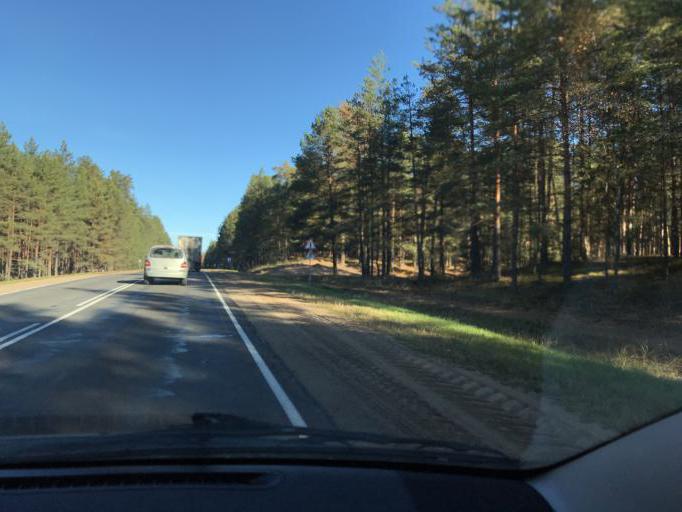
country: BY
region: Vitebsk
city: Polatsk
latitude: 55.3446
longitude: 28.7963
